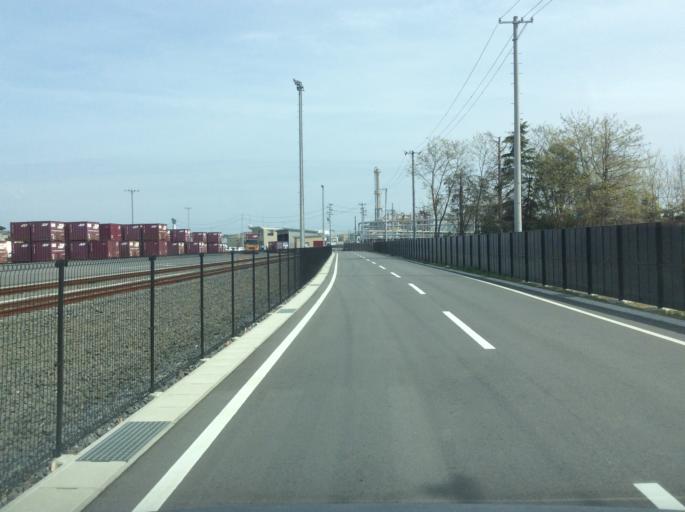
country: JP
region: Fukushima
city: Iwaki
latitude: 36.9476
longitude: 140.8969
